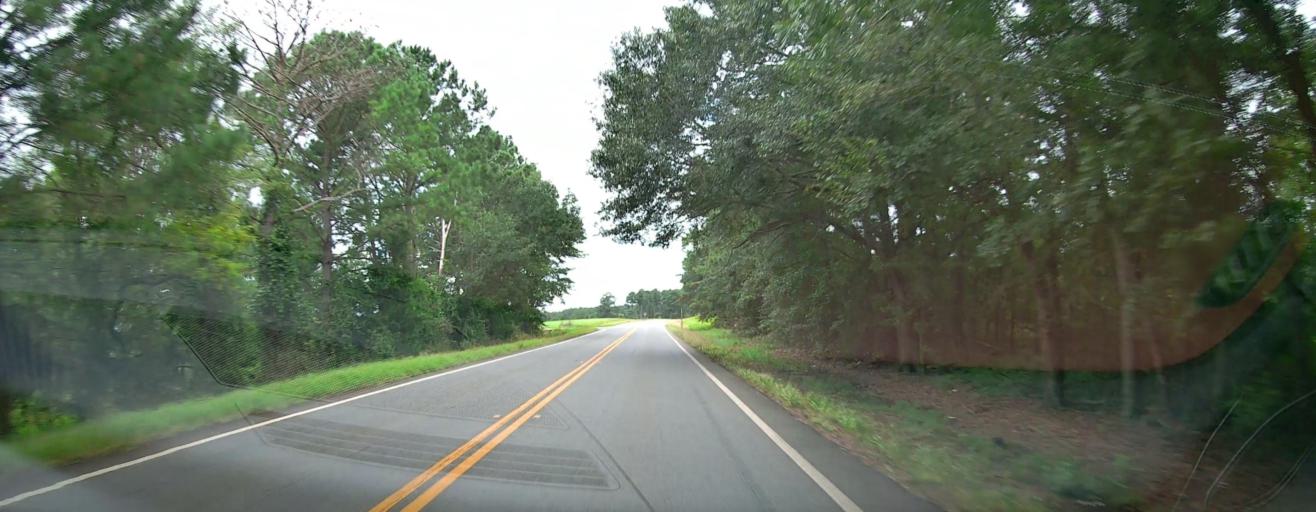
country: US
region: Georgia
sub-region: Marion County
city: Buena Vista
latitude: 32.2615
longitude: -84.4248
